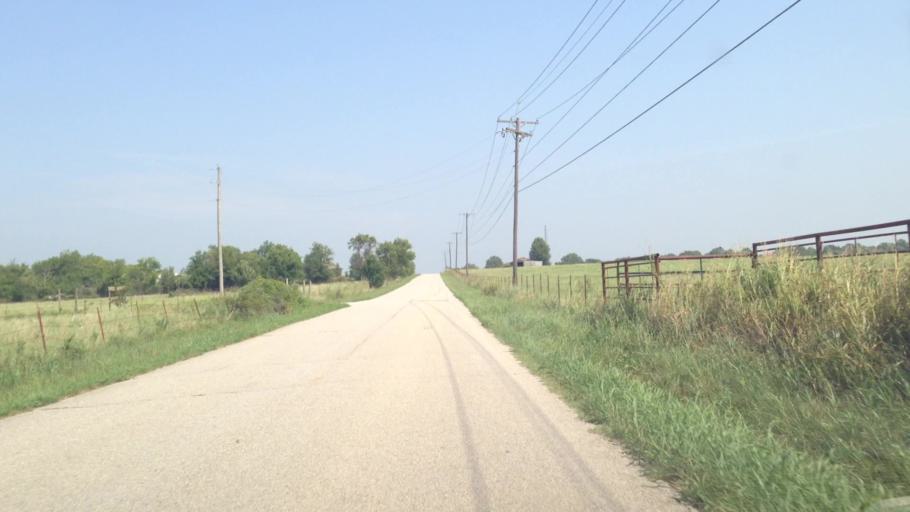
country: US
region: Oklahoma
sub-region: Craig County
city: Vinita
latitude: 36.6485
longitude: -95.1256
